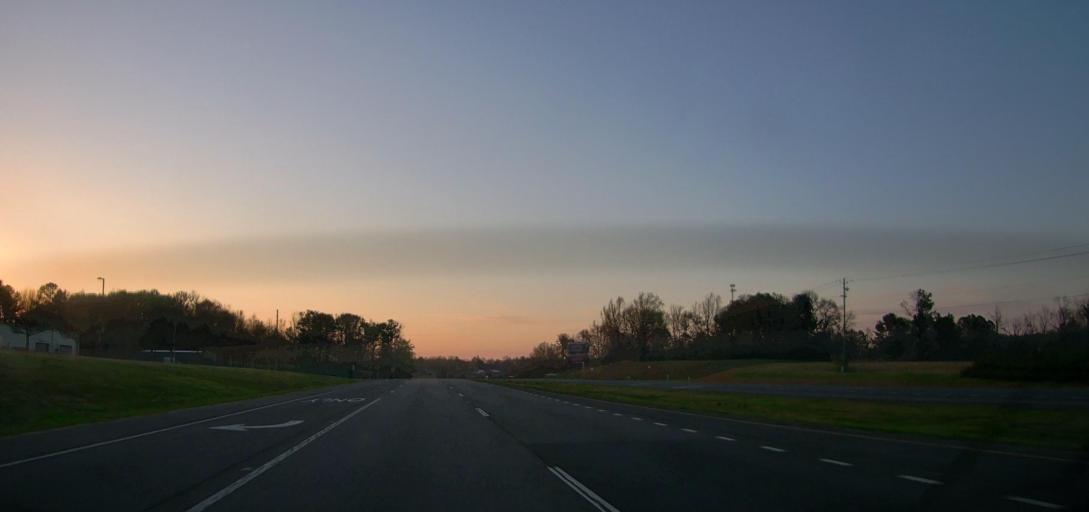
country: US
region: Alabama
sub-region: Tallapoosa County
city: Alexander City
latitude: 32.9642
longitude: -86.0063
